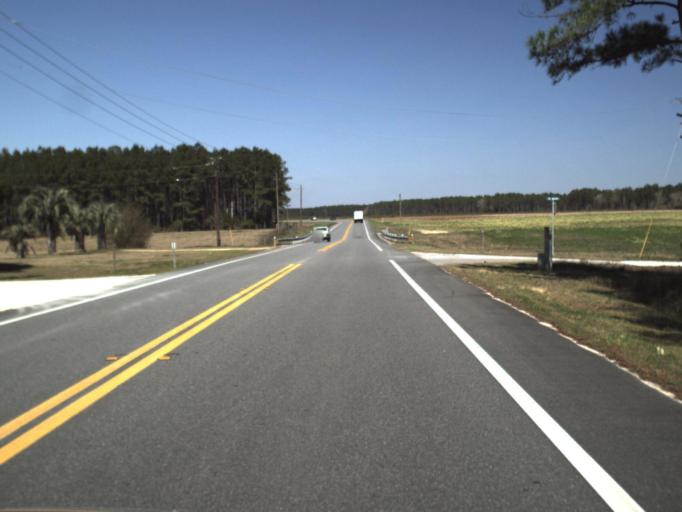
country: US
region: Florida
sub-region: Gulf County
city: Wewahitchka
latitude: 30.2149
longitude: -85.2065
